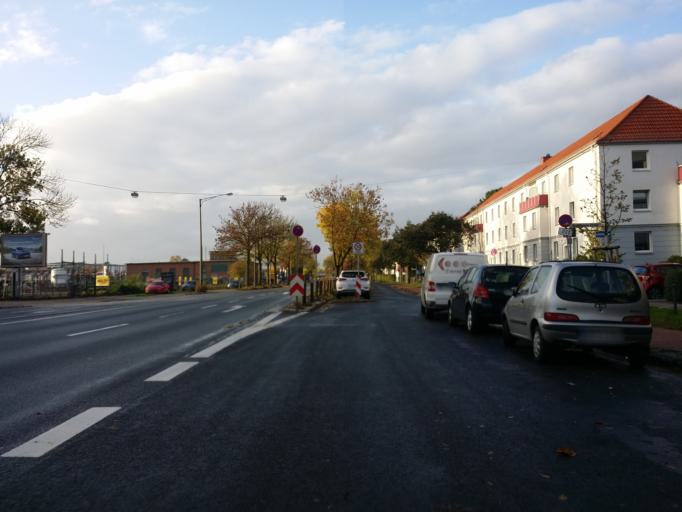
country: DE
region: Bremen
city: Bremen
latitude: 53.0633
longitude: 8.7876
